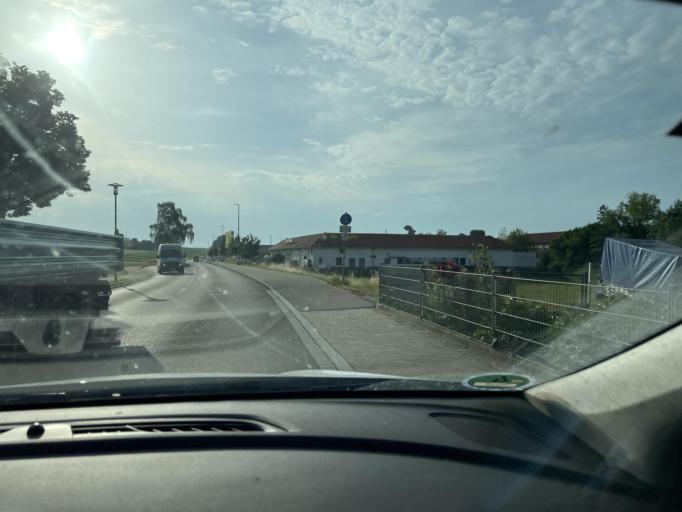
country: DE
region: Bavaria
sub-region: Swabia
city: Aindling
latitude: 48.5125
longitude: 10.9638
